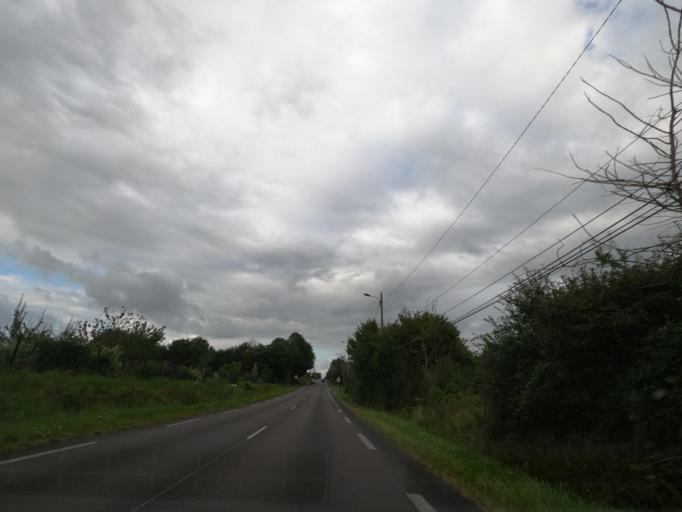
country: FR
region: Haute-Normandie
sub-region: Departement de l'Eure
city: Bourgtheroulde-Infreville
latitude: 49.3113
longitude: 0.8894
